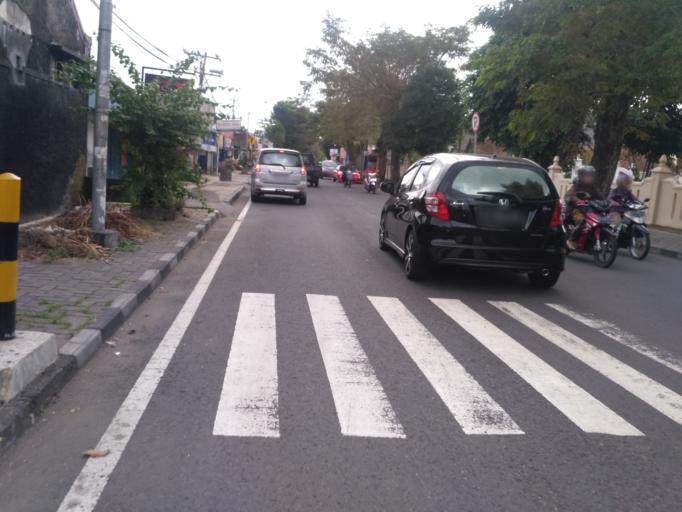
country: ID
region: Daerah Istimewa Yogyakarta
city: Melati
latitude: -7.7409
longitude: 110.3627
